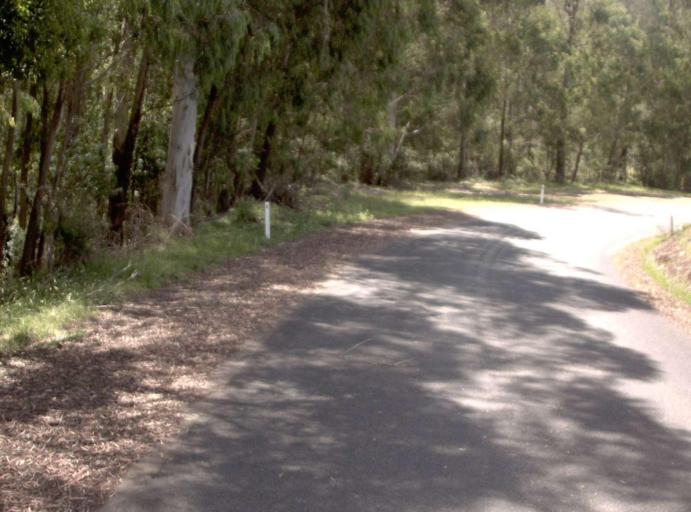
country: AU
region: New South Wales
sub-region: Bombala
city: Bombala
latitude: -37.4340
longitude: 148.9894
